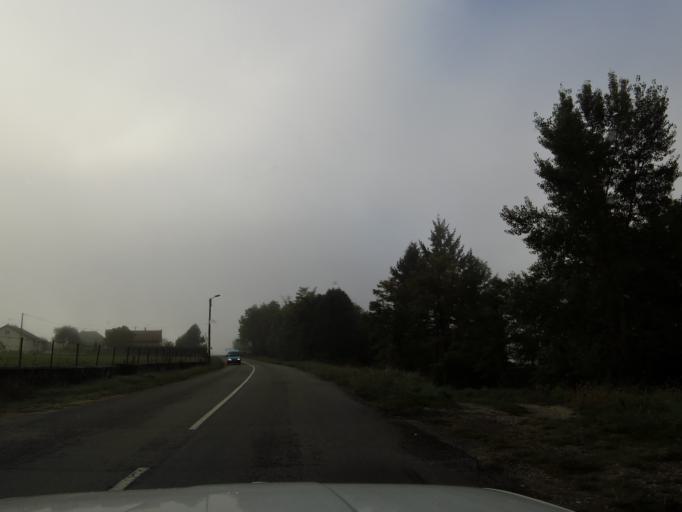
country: FR
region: Rhone-Alpes
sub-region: Departement de l'Isere
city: Creys-Mepieu
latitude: 45.7813
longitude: 5.4691
